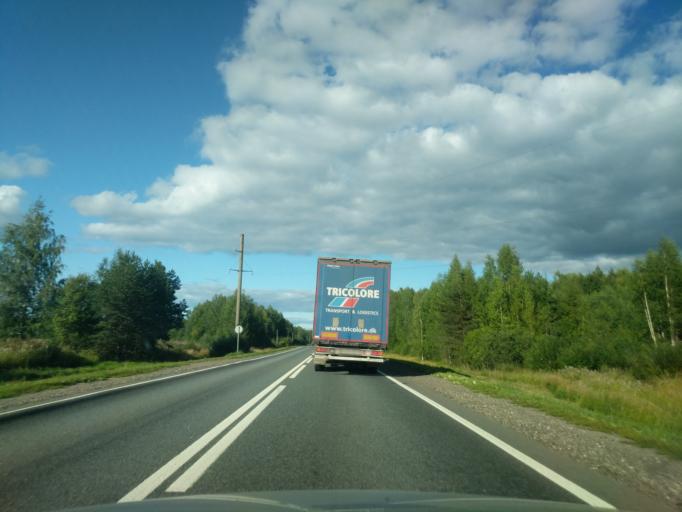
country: RU
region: Kostroma
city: Manturovo
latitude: 58.1464
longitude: 44.3666
